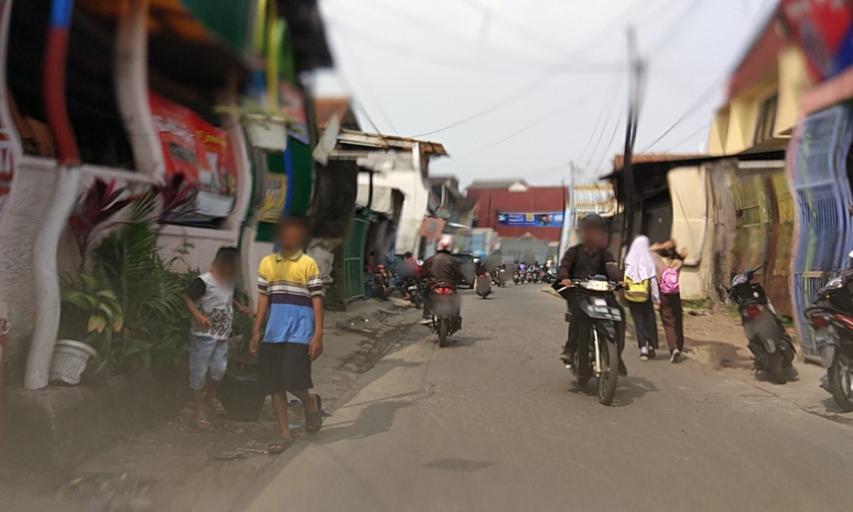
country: ID
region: West Java
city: Margahayukencana
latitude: -6.9352
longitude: 107.5845
